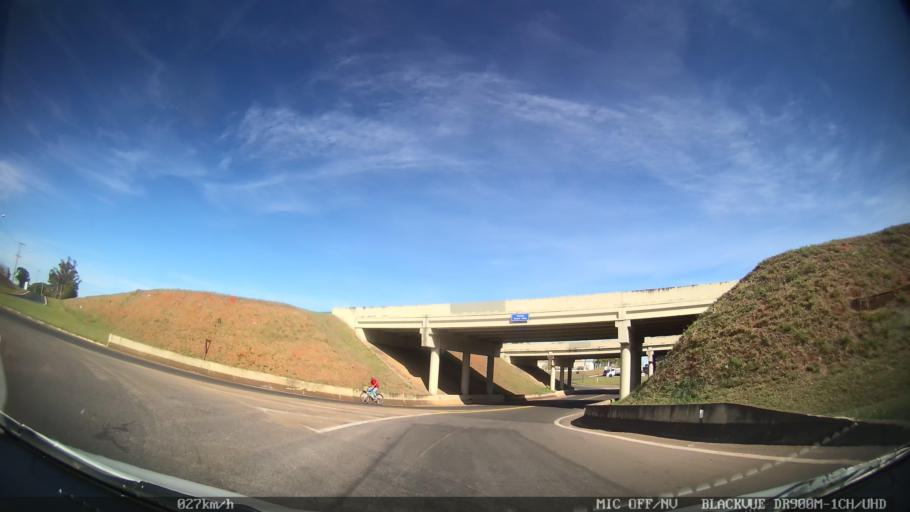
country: BR
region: Sao Paulo
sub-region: Leme
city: Leme
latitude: -22.2029
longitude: -47.3952
